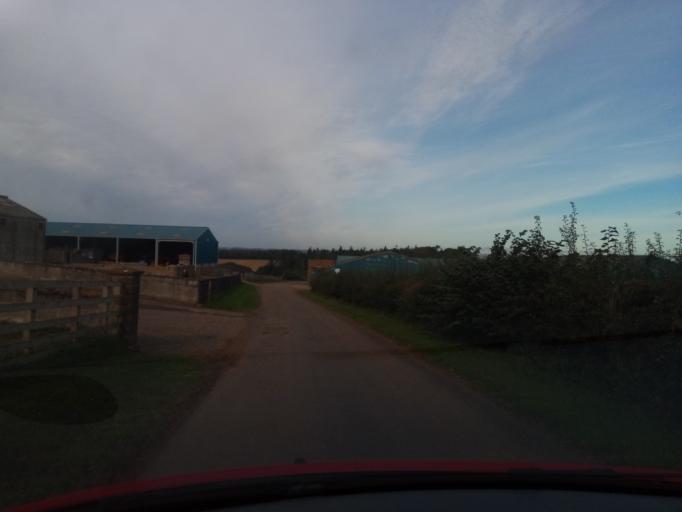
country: GB
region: Scotland
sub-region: The Scottish Borders
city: Kelso
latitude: 55.5808
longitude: -2.3682
